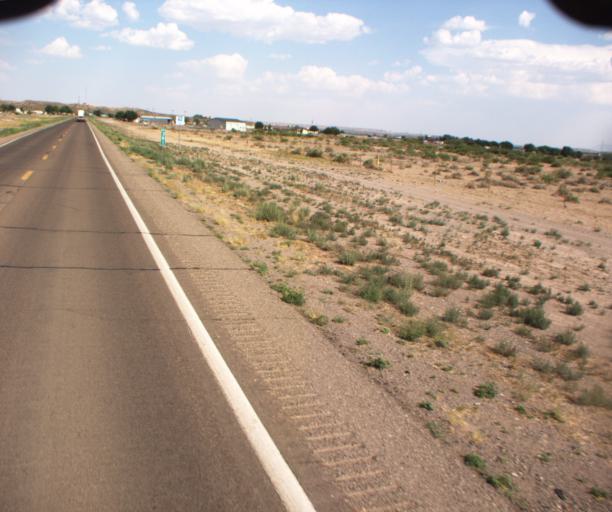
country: US
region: Arizona
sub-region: Greenlee County
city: Clifton
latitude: 32.7439
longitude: -109.1014
